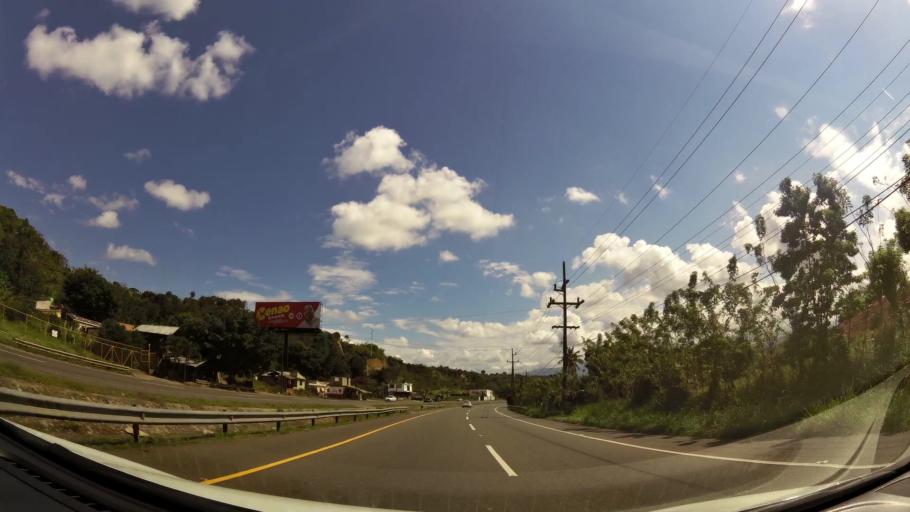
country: DO
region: La Vega
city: Rio Verde Arriba
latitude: 19.2795
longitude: -70.5706
